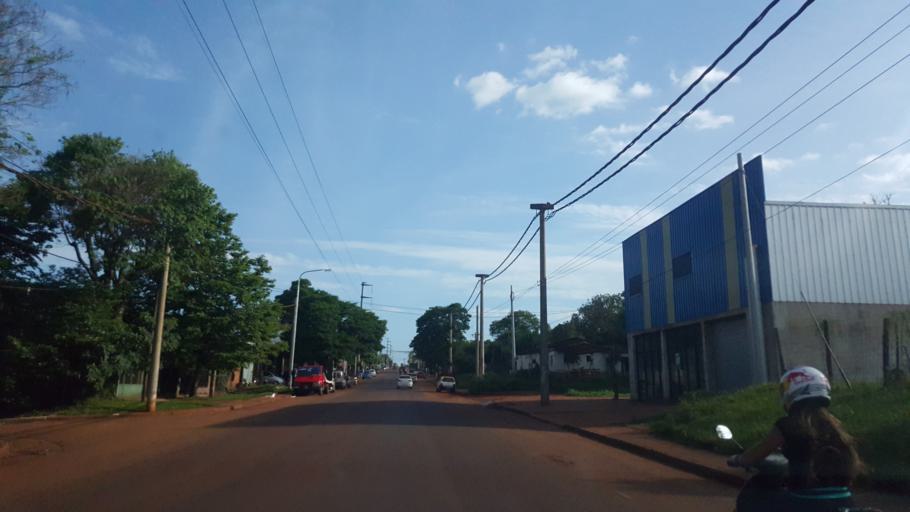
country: AR
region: Misiones
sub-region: Departamento de Capital
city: Posadas
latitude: -27.4222
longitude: -55.9135
